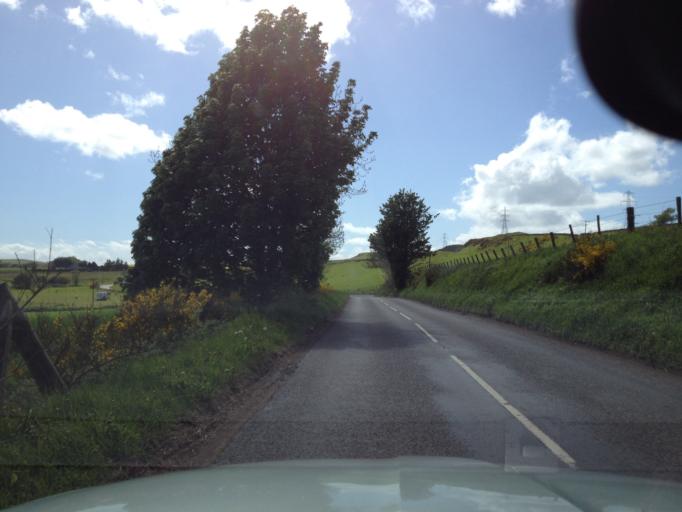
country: GB
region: Scotland
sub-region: Angus
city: Letham
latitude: 56.6895
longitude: -2.7848
